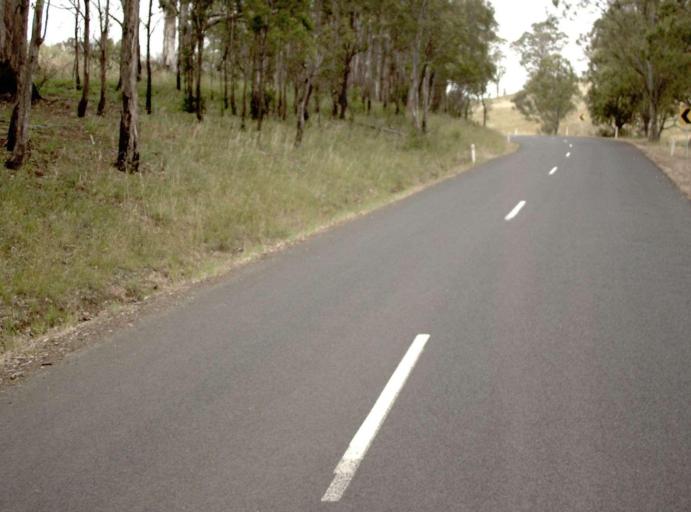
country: AU
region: Victoria
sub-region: Wellington
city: Heyfield
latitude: -37.8946
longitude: 146.7243
